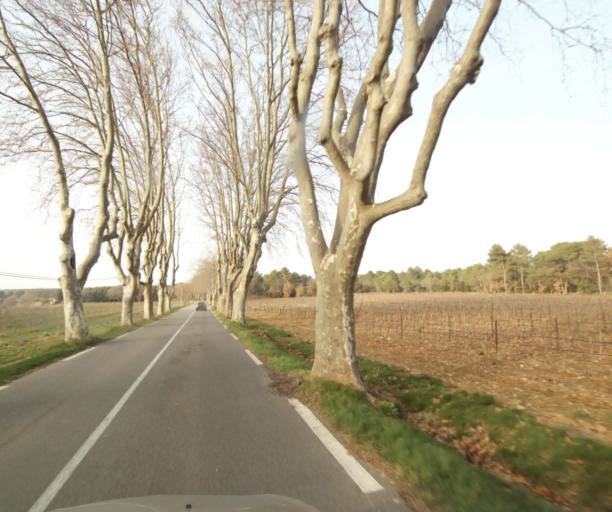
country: FR
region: Provence-Alpes-Cote d'Azur
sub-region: Departement des Bouches-du-Rhone
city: Eguilles
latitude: 43.6076
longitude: 5.3656
